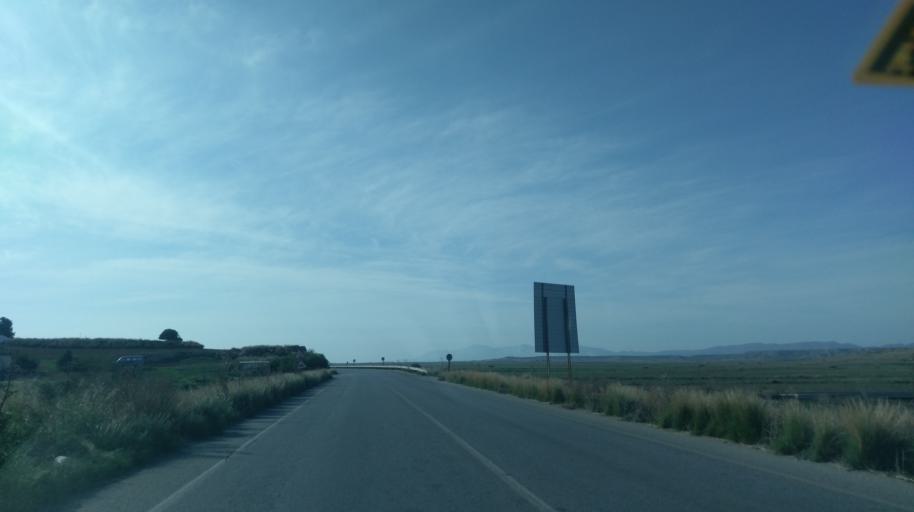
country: CY
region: Ammochostos
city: Trikomo
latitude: 35.2749
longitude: 33.8278
